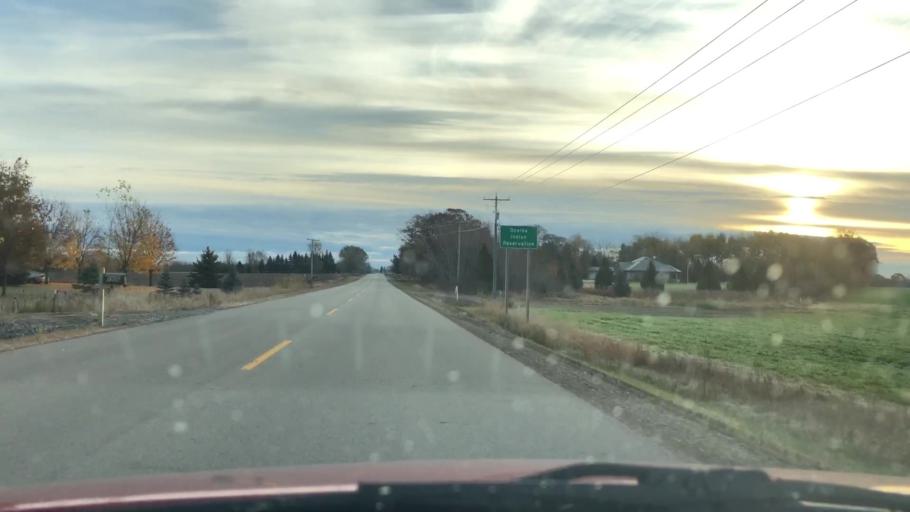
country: US
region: Wisconsin
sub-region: Outagamie County
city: Seymour
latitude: 44.4153
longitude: -88.2783
